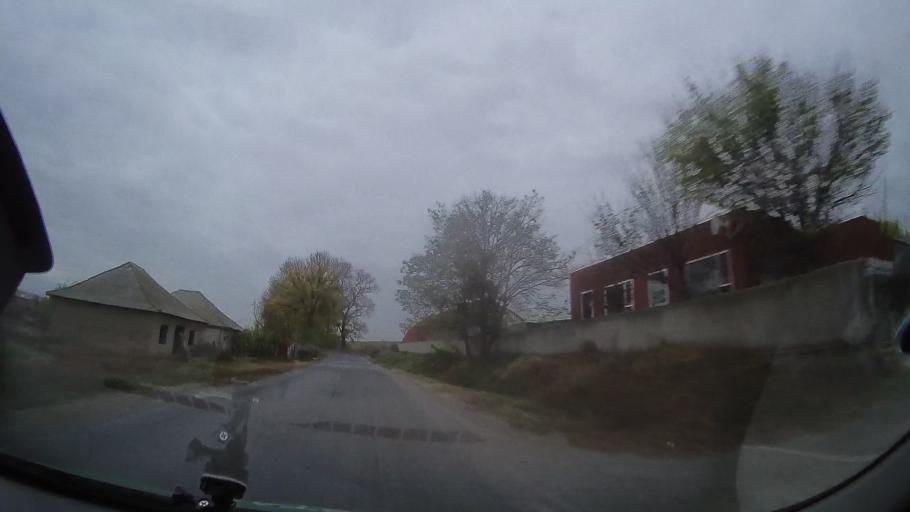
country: RO
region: Tulcea
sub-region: Comuna Mihai Bravu
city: Turda
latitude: 44.9676
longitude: 28.6304
